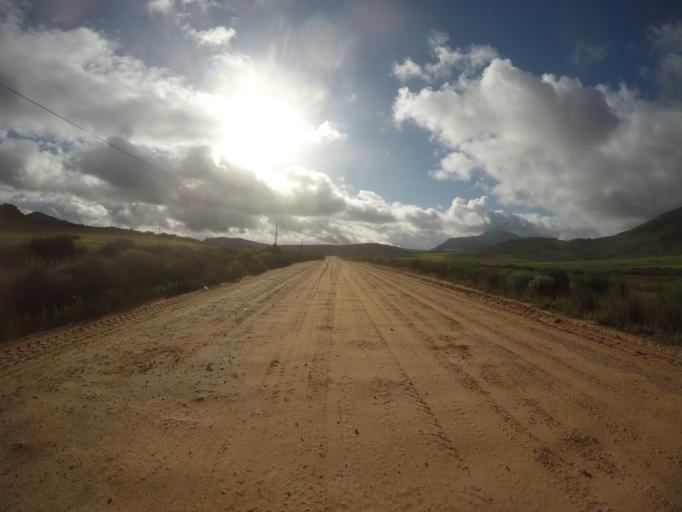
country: ZA
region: Western Cape
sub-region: West Coast District Municipality
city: Clanwilliam
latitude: -32.3431
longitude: 18.8265
